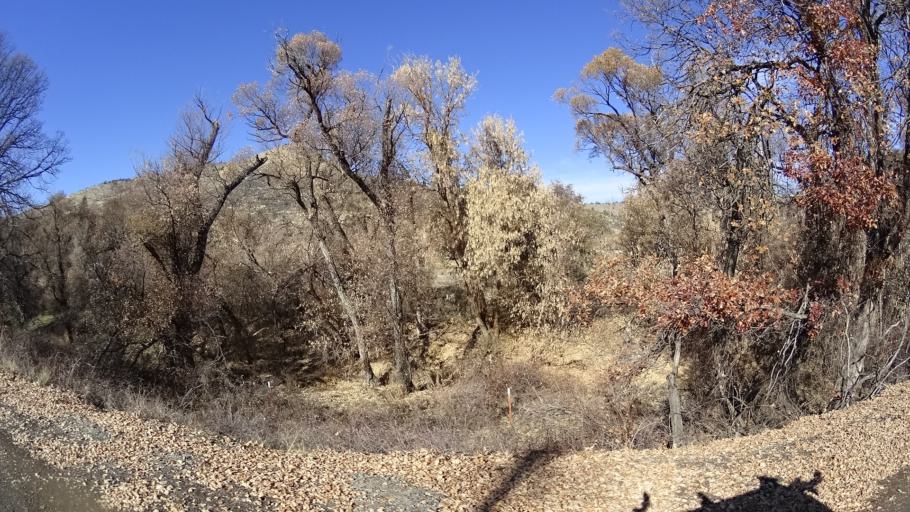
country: US
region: California
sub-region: Siskiyou County
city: Yreka
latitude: 41.7721
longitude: -122.6026
